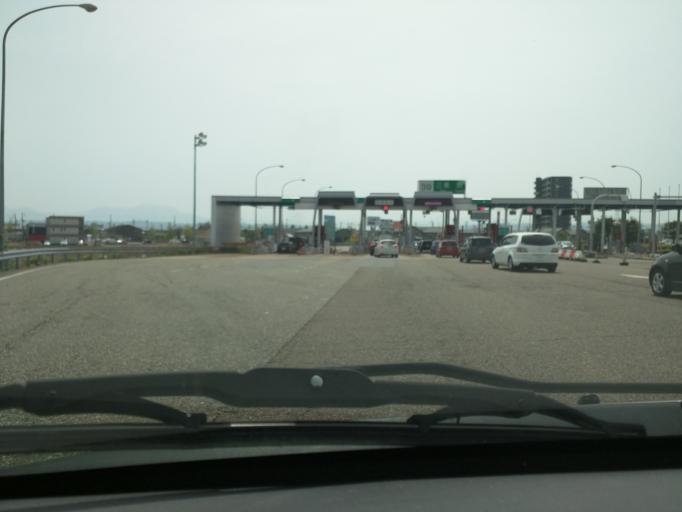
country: JP
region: Niigata
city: Tsubame
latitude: 37.6519
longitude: 138.9414
